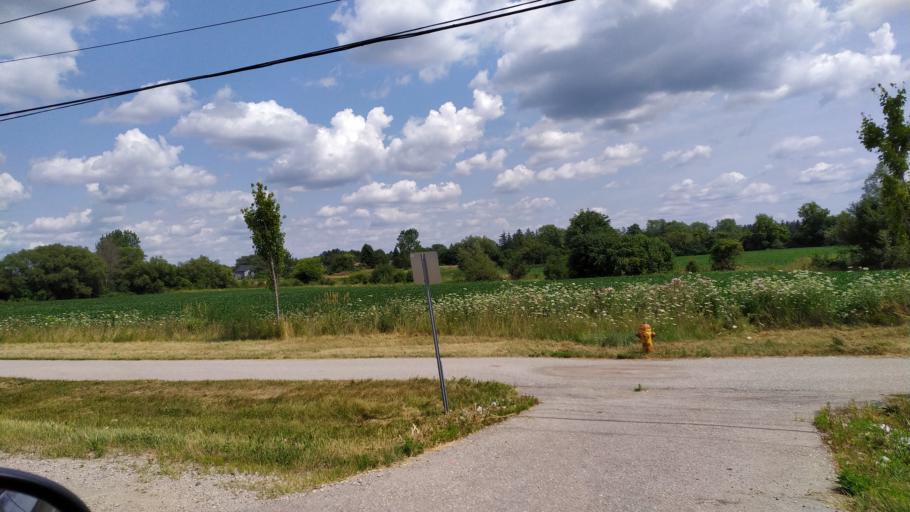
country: CA
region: Ontario
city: Stratford
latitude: 43.3757
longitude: -81.0087
